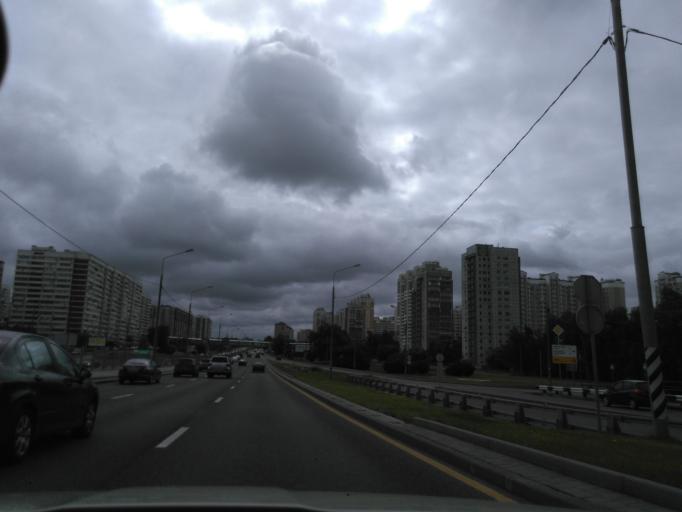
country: RU
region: Moskovskaya
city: Bol'shaya Setun'
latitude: 55.7450
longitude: 37.4215
